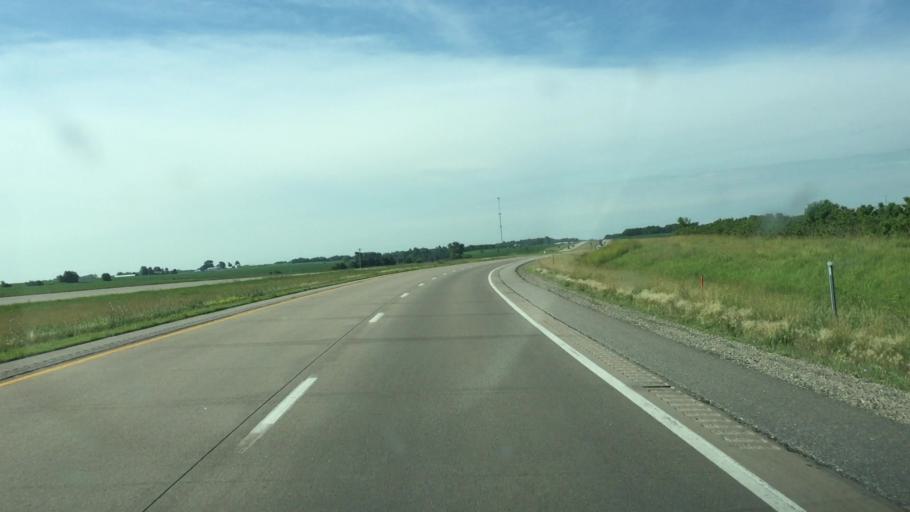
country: US
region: Iowa
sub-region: Henry County
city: Winfield
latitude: 41.2316
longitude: -91.5296
